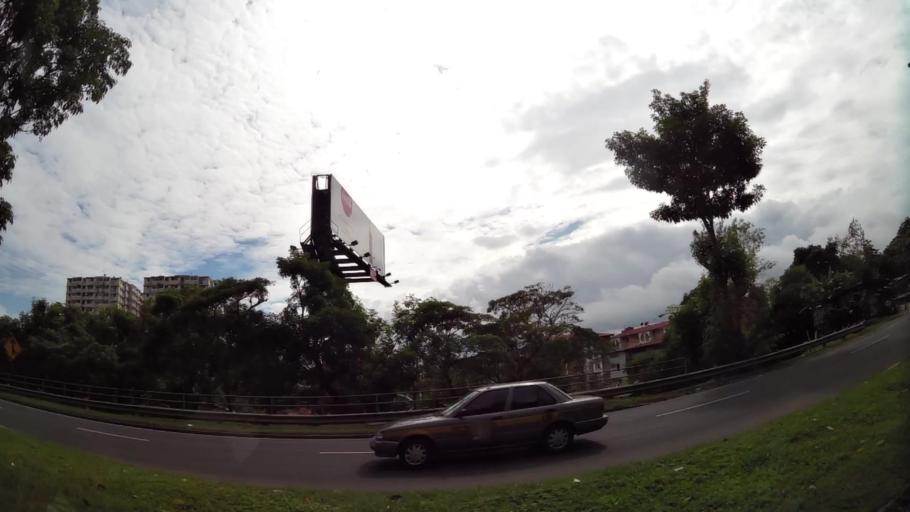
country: PA
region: Panama
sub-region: Distrito de Panama
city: Ancon
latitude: 8.9494
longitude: -79.5493
